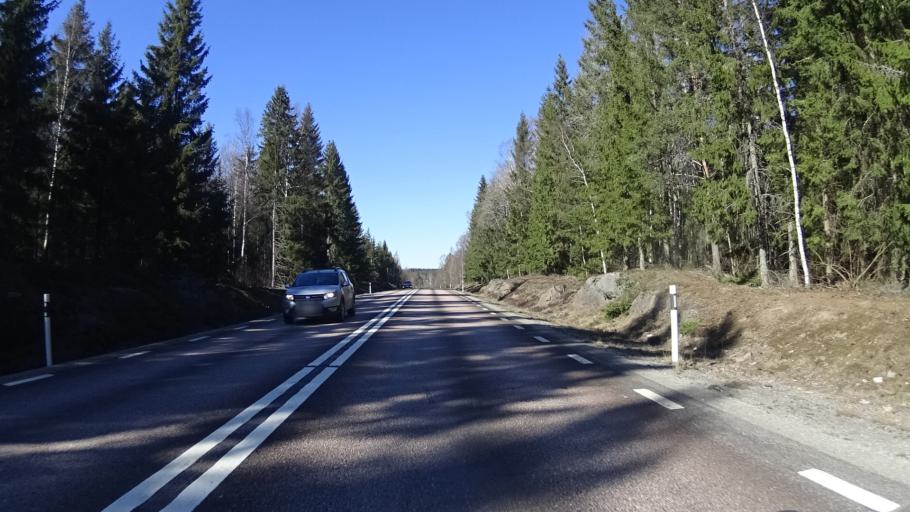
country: SE
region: Vaermland
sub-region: Sunne Kommun
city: Sunne
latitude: 59.6393
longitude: 12.9457
